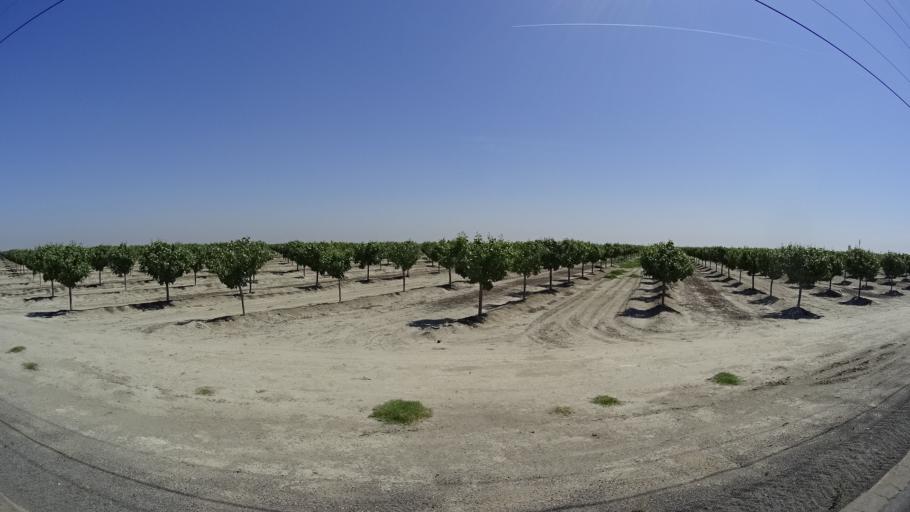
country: US
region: California
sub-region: Kings County
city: Corcoran
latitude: 36.0744
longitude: -119.5391
